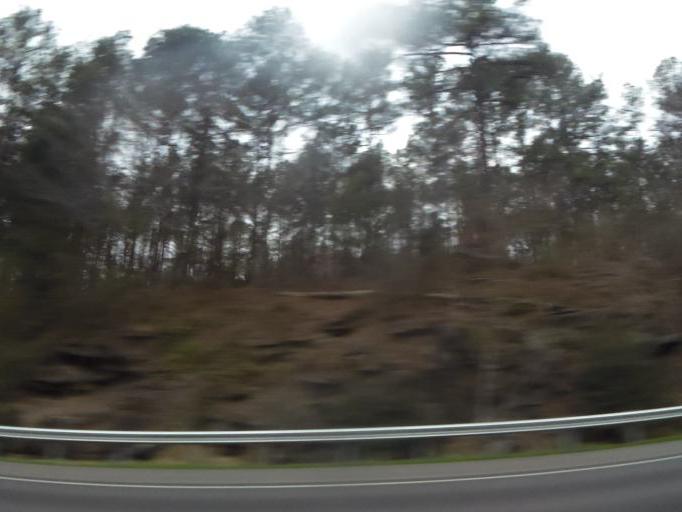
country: US
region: Alabama
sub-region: Jefferson County
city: Warrior
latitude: 33.8403
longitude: -86.8248
